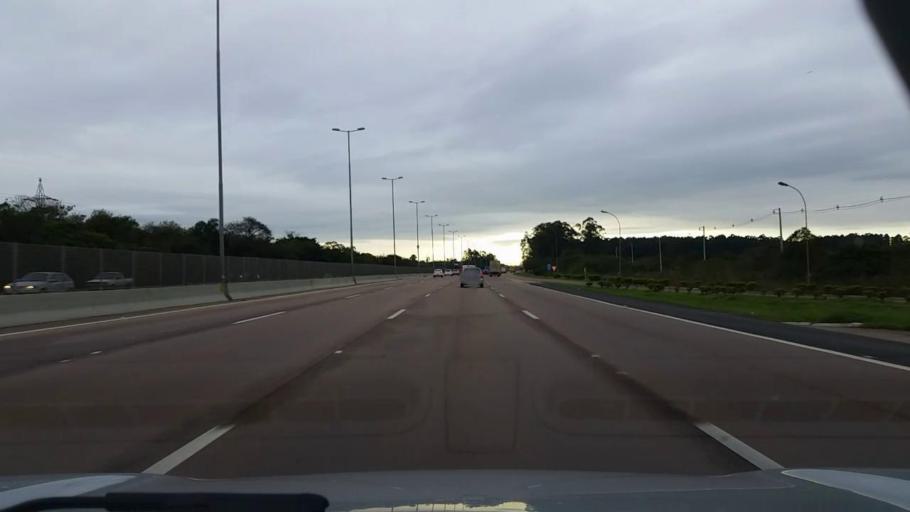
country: BR
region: Rio Grande do Sul
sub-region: Cachoeirinha
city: Cachoeirinha
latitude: -29.9531
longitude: -51.0492
